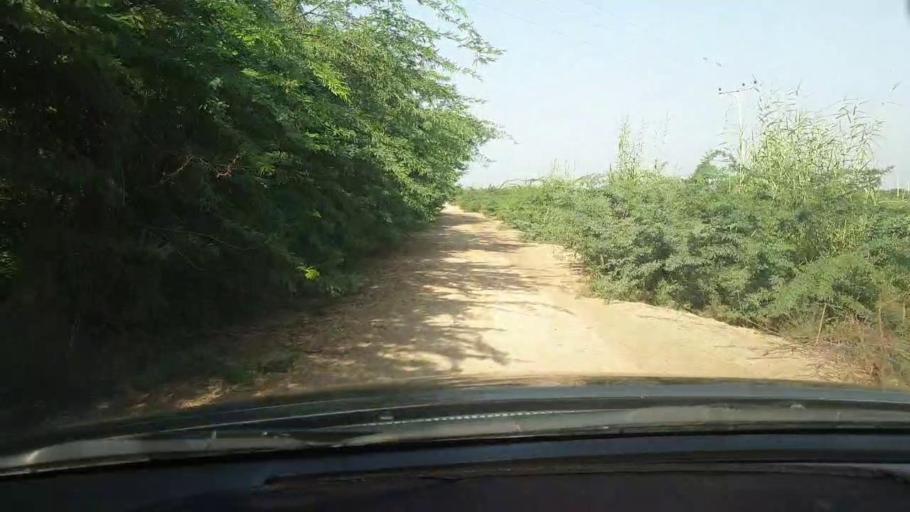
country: PK
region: Sindh
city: Tando Bago
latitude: 24.6741
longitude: 69.1740
